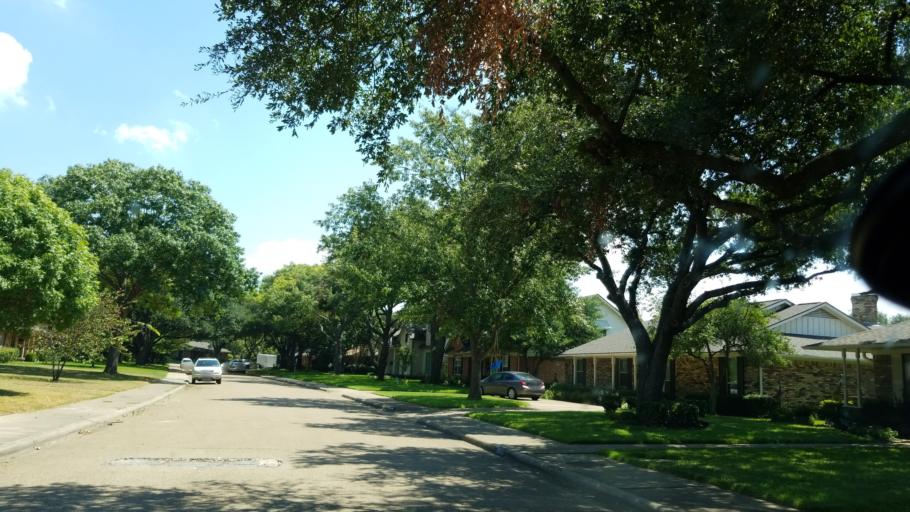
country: US
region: Texas
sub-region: Dallas County
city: Richardson
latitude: 32.8914
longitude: -96.7148
